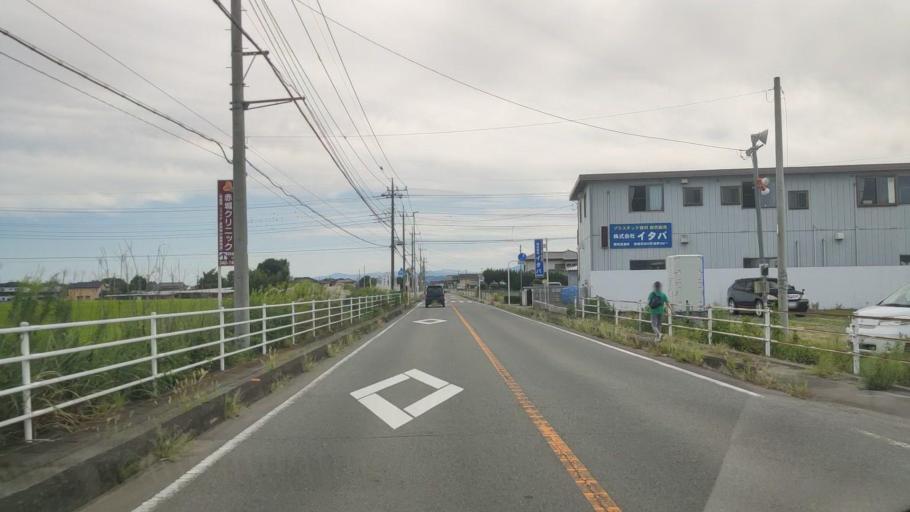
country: JP
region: Gunma
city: Kanekomachi
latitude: 36.3703
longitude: 138.9738
